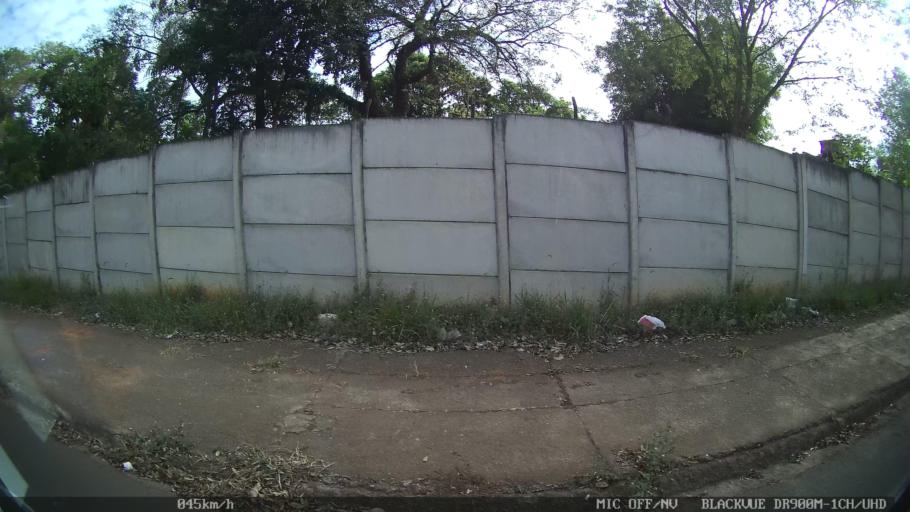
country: BR
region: Sao Paulo
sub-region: Santa Barbara D'Oeste
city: Santa Barbara d'Oeste
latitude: -22.7734
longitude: -47.4031
